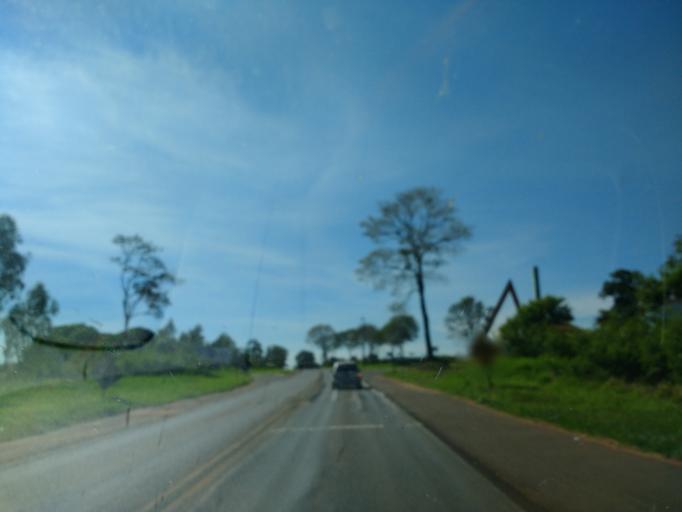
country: BR
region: Parana
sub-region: Alto Piquiri
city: Alto Piquiri
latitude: -23.8902
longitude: -53.4093
